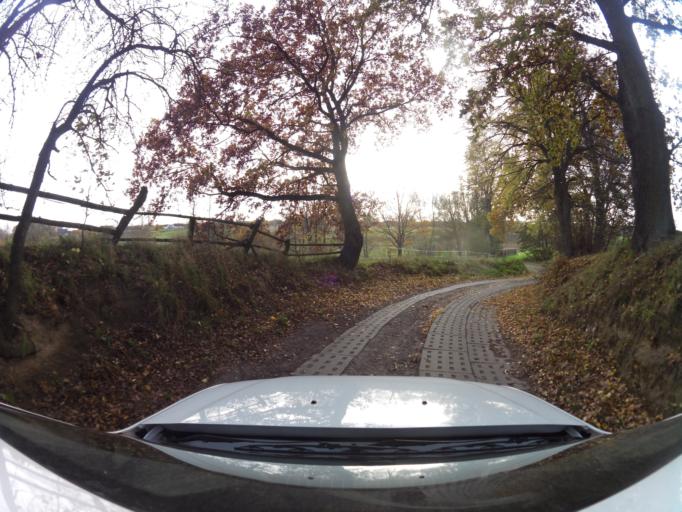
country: PL
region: West Pomeranian Voivodeship
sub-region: Powiat gryficki
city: Gryfice
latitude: 53.8203
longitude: 15.1271
